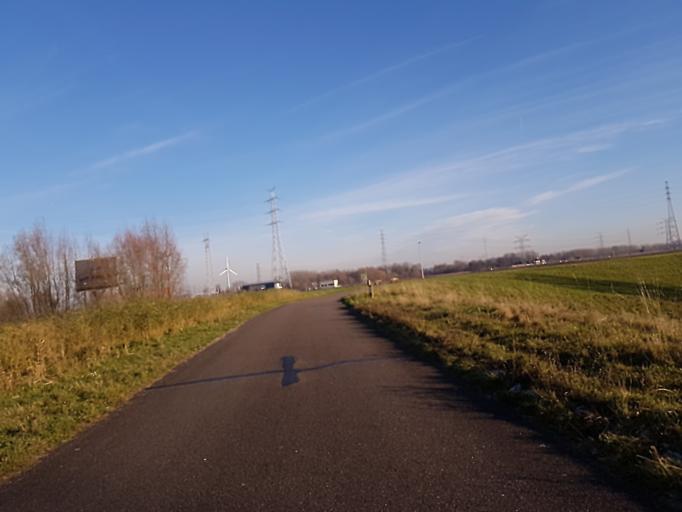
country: BE
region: Flanders
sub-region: Provincie Antwerpen
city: Niel
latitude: 51.1218
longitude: 4.3010
